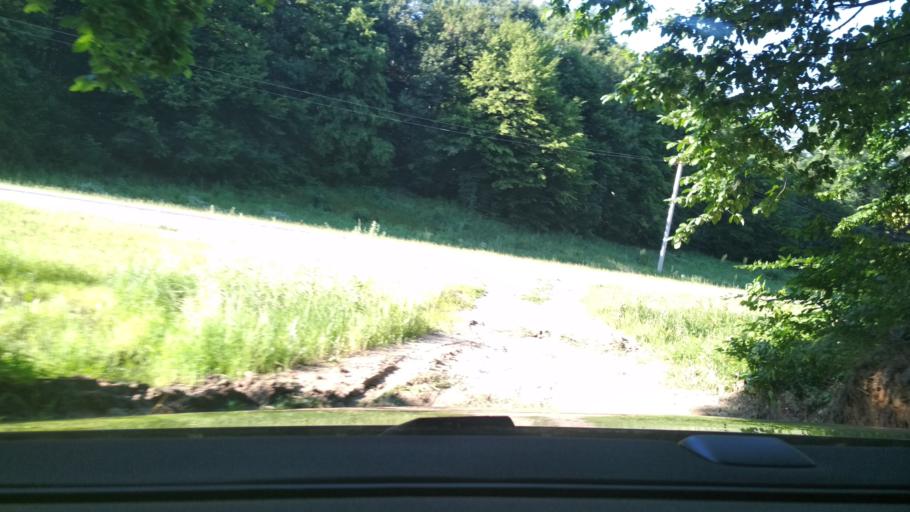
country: MD
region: Stinga Nistrului
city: Bucovat
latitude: 47.0816
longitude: 28.3712
